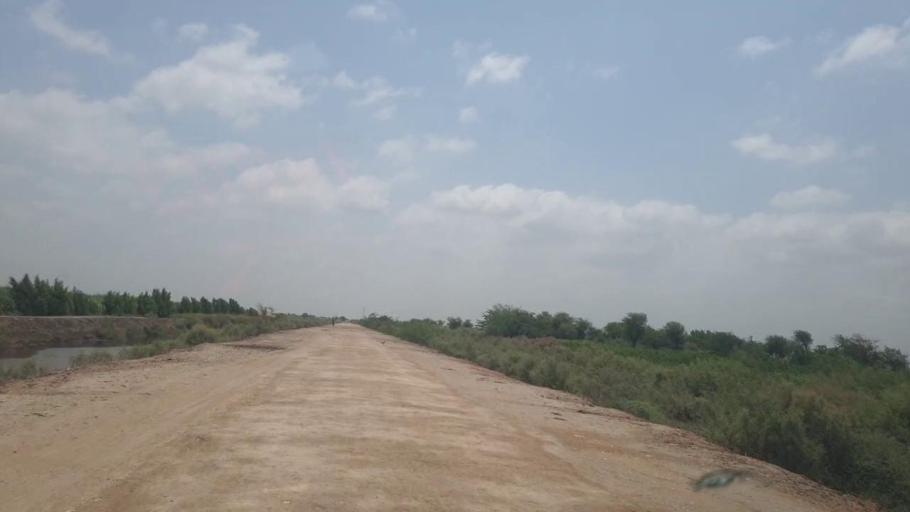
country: PK
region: Sindh
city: Tando Mittha Khan
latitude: 25.9181
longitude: 69.1996
